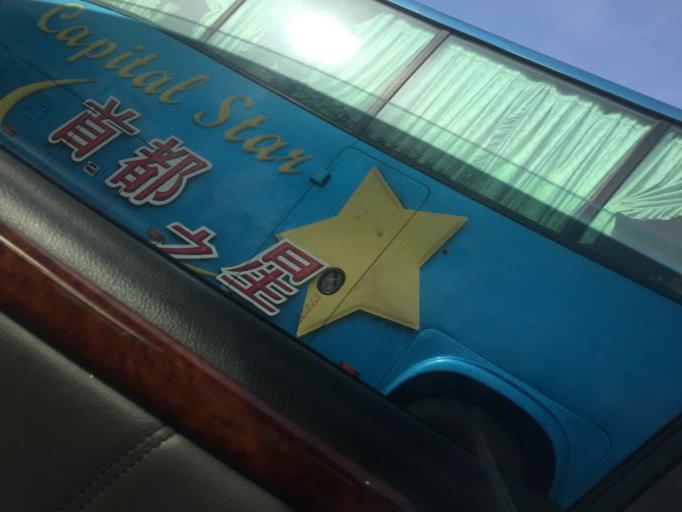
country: TW
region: Taiwan
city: Daxi
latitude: 24.8643
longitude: 121.2227
